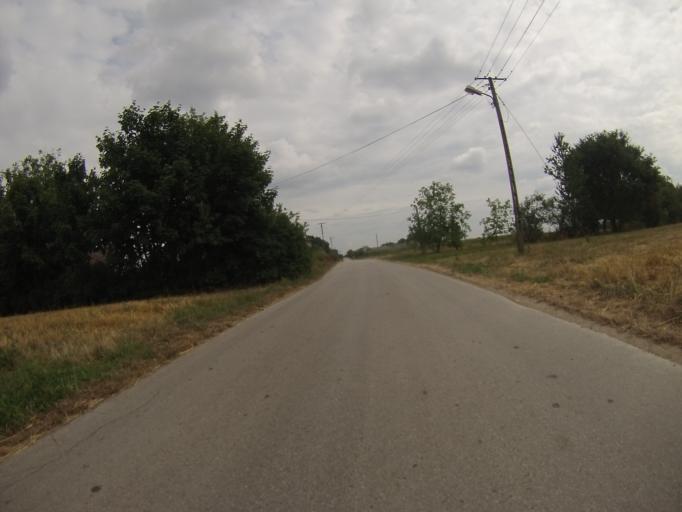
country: PL
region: Swietokrzyskie
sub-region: Powiat kielecki
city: Lagow
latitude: 50.7193
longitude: 21.1182
